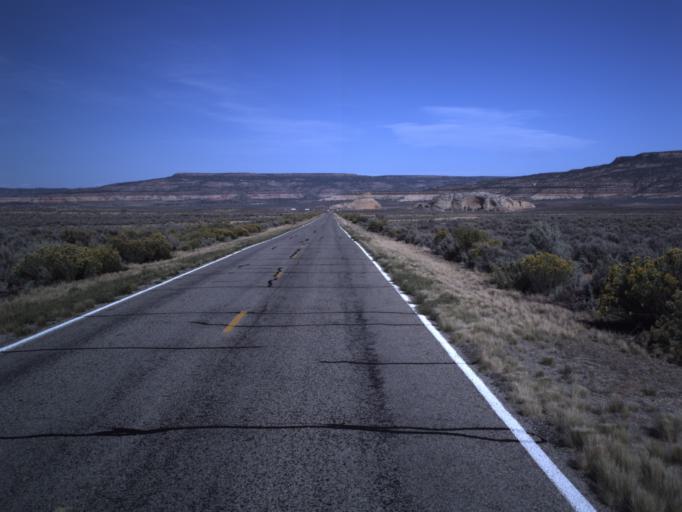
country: US
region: Utah
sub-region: San Juan County
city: Monticello
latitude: 38.0636
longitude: -109.3899
